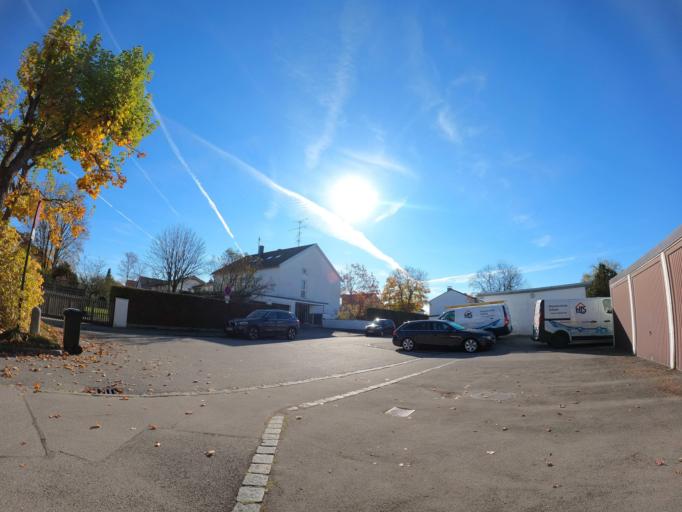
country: DE
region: Bavaria
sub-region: Upper Bavaria
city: Oberhaching
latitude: 48.0245
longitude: 11.6024
